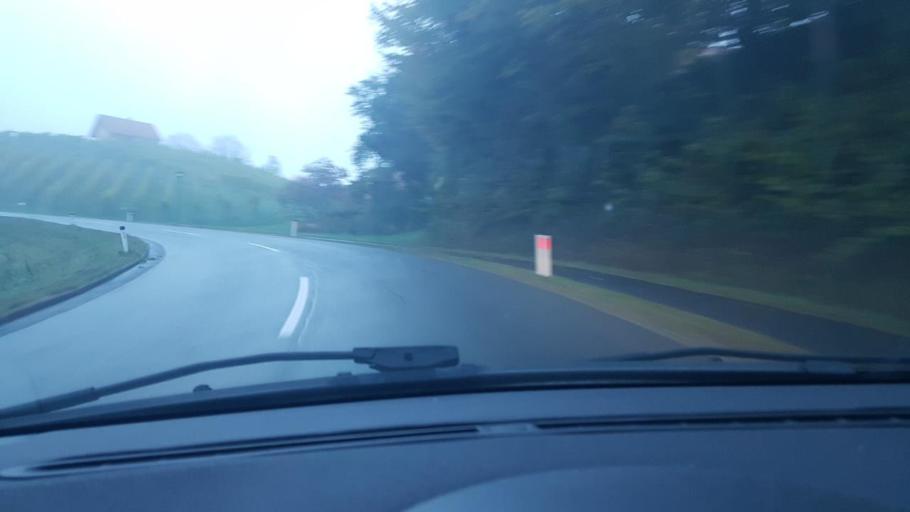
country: AT
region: Styria
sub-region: Politischer Bezirk Leibnitz
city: Sulztal an der Weinstrasse
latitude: 46.6740
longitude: 15.5383
